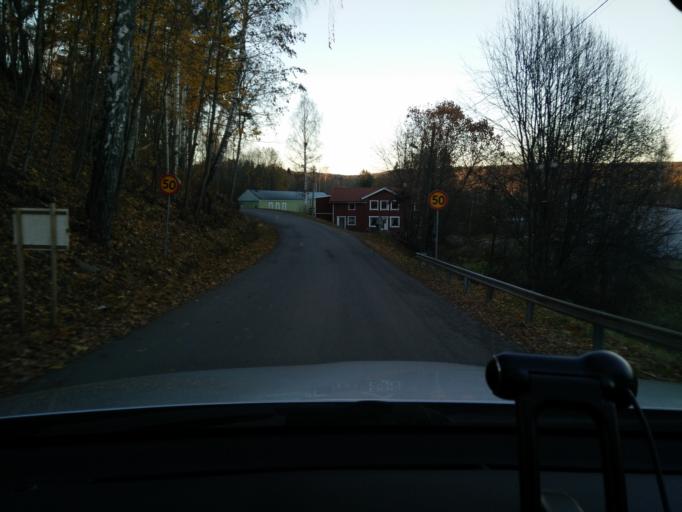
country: SE
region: Vaesternorrland
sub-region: Sundsvalls Kommun
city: Matfors
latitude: 62.3490
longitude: 17.0232
